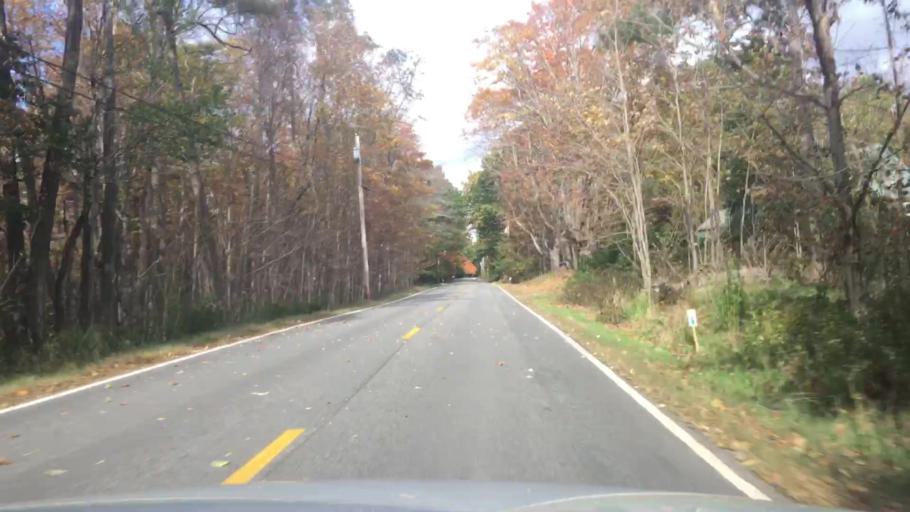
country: US
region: Maine
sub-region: Knox County
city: Hope
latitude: 44.3159
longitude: -69.1219
